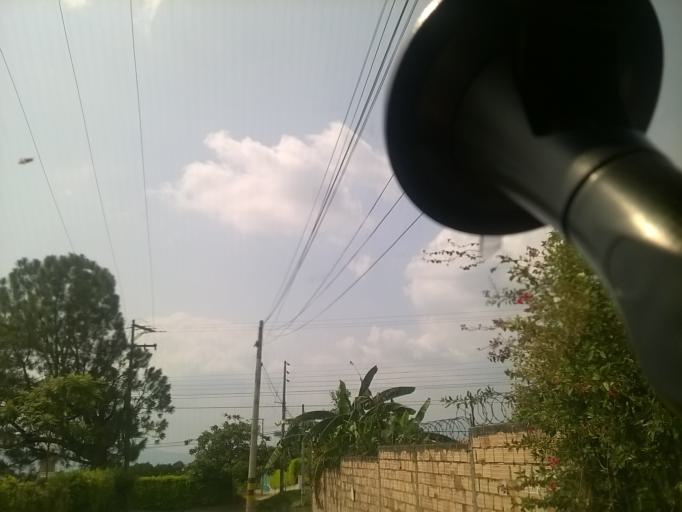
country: CO
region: Cundinamarca
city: San Antonio del Tequendama
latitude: 4.6384
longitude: -74.4476
